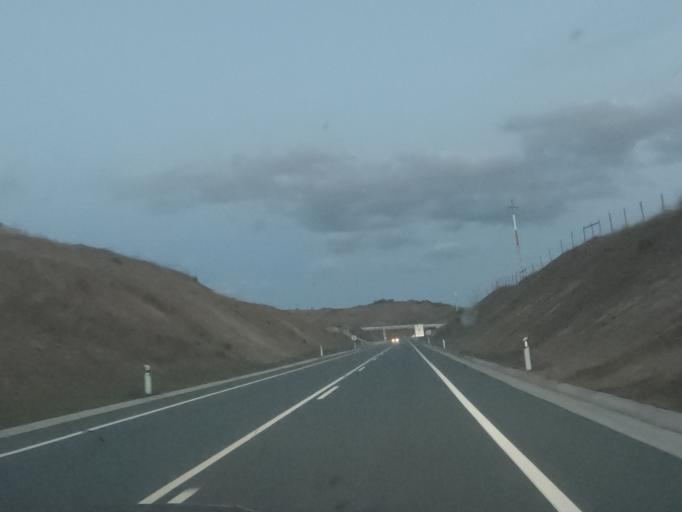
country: PT
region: Braganca
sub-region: Alfandega da Fe
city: Alfandega da Fe
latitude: 41.3302
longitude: -6.9573
